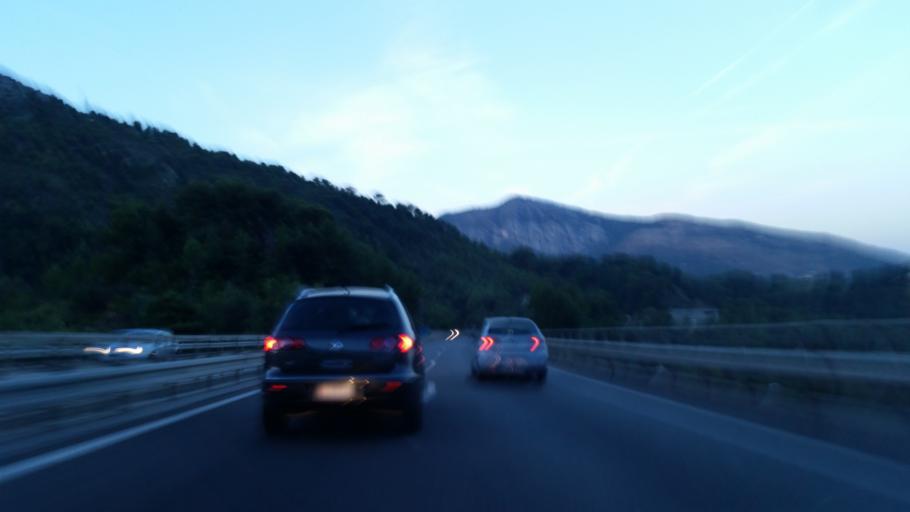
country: FR
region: Provence-Alpes-Cote d'Azur
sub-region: Departement des Alpes-Maritimes
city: Gorbio
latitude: 43.7821
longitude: 7.4505
